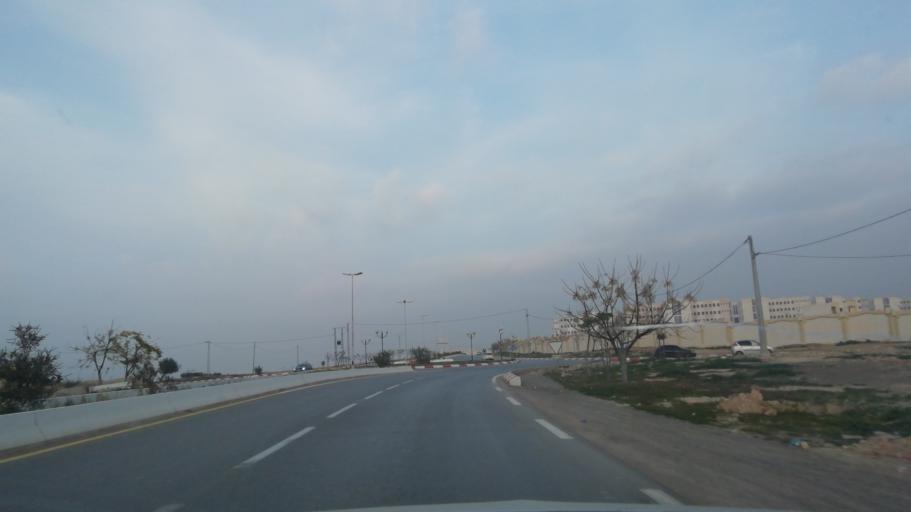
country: DZ
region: Sidi Bel Abbes
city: Sidi Bel Abbes
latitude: 35.2170
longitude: -0.6510
